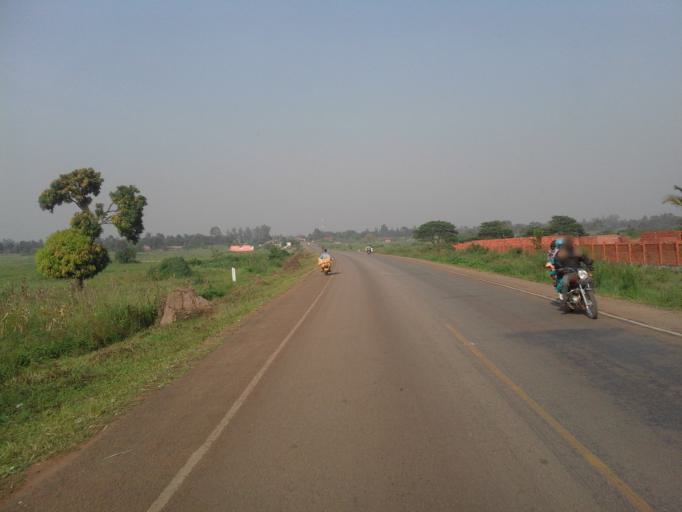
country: UG
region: Eastern Region
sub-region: Mbale District
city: Mbale
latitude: 1.0759
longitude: 34.1081
